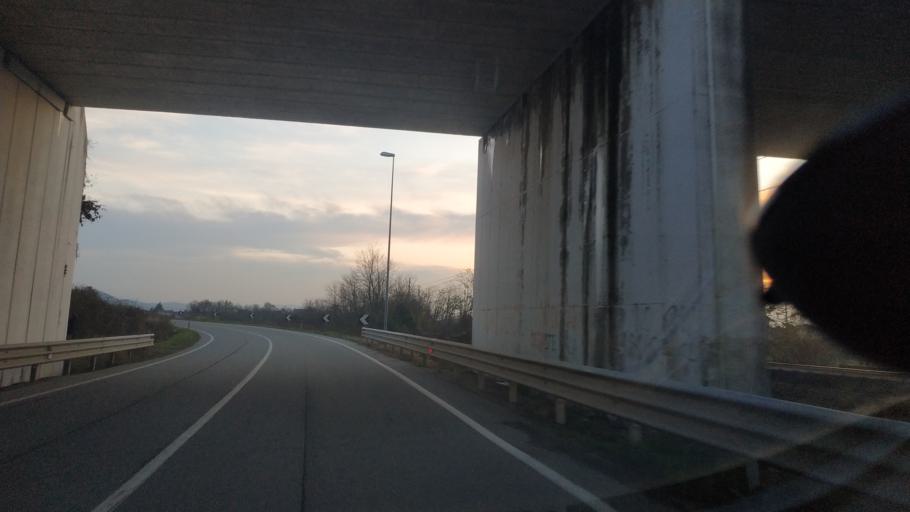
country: IT
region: Piedmont
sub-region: Provincia di Torino
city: Montanaro
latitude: 45.2417
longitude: 7.8613
